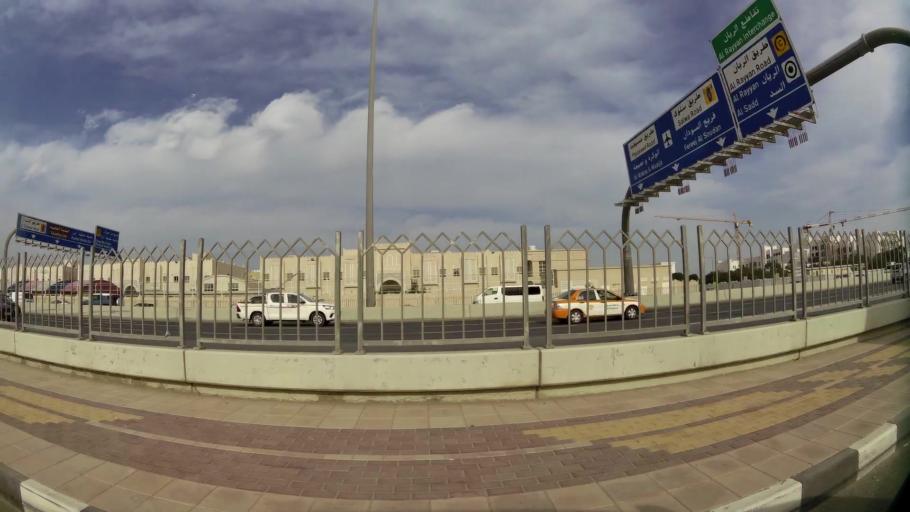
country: QA
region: Baladiyat ar Rayyan
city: Ar Rayyan
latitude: 25.3042
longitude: 51.4730
